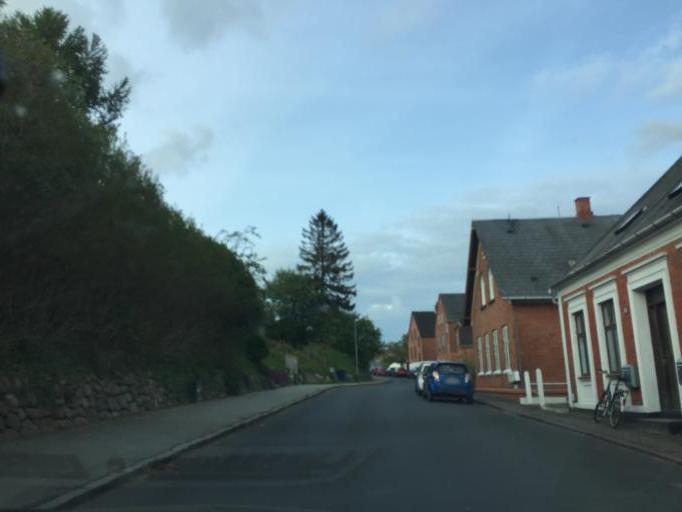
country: DK
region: South Denmark
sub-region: Svendborg Kommune
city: Svendborg
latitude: 55.0642
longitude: 10.6067
